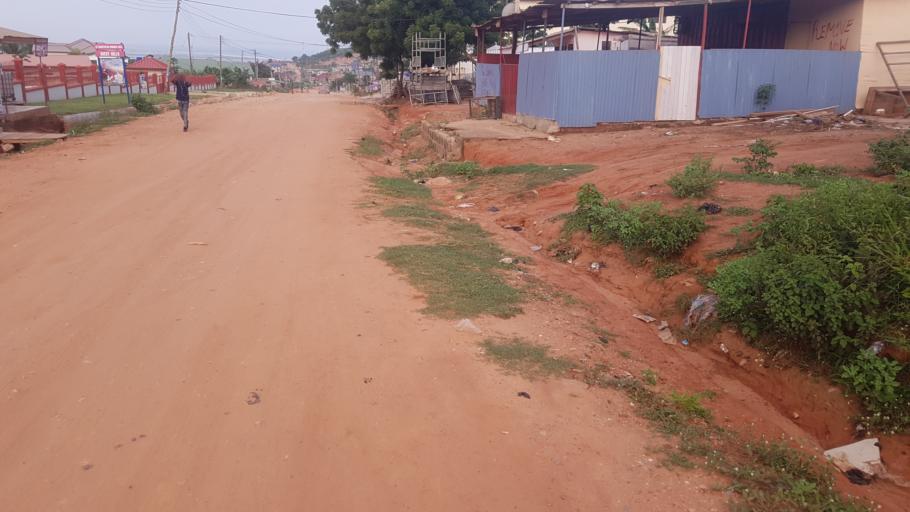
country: GH
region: Greater Accra
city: Gbawe
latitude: 5.5243
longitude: -0.3475
